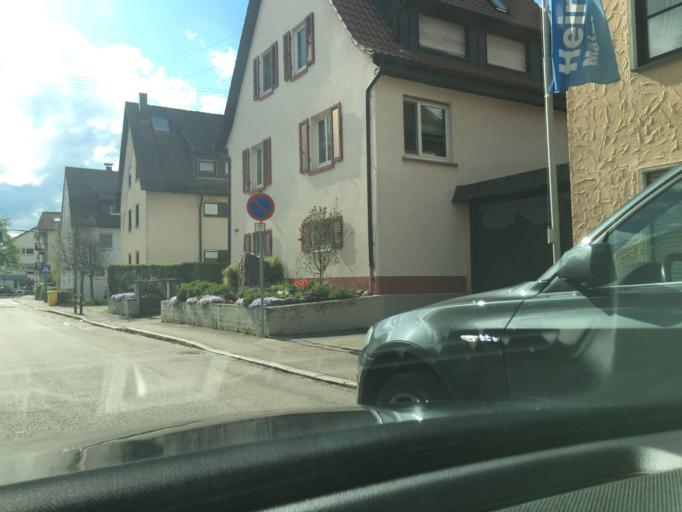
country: DE
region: Baden-Wuerttemberg
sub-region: Regierungsbezirk Stuttgart
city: Stuttgart Muehlhausen
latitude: 48.8440
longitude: 9.2660
